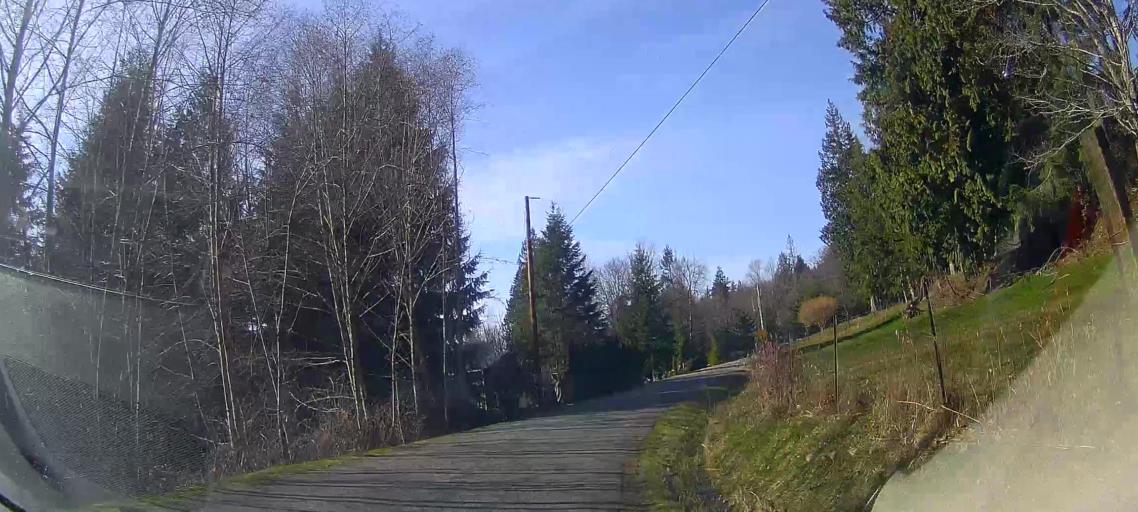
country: US
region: Washington
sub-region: Skagit County
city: Burlington
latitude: 48.5892
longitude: -122.3715
